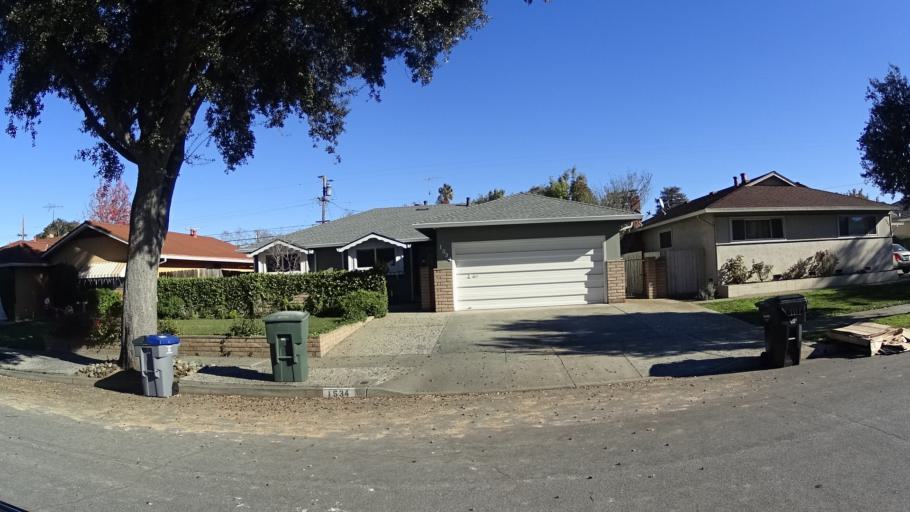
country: US
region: California
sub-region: Santa Clara County
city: Cupertino
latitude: 37.3442
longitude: -122.0152
